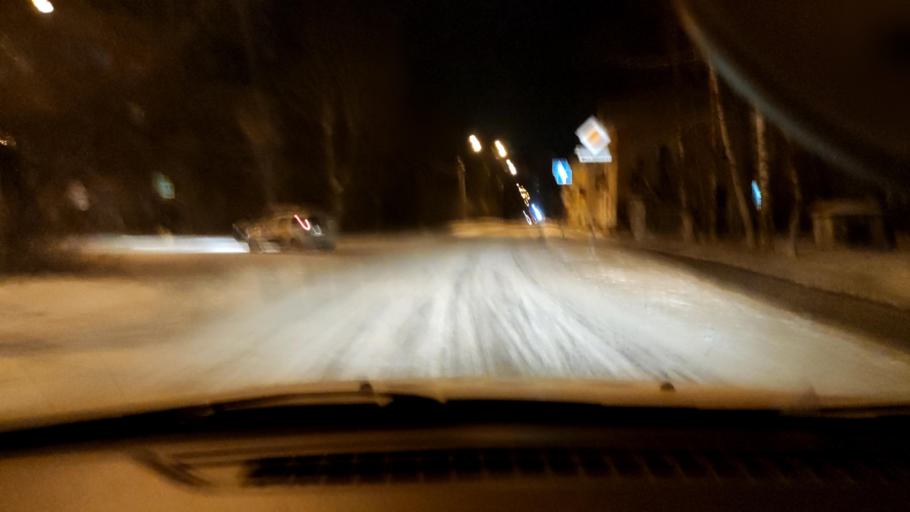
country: RU
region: Perm
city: Kultayevo
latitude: 58.0059
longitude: 55.9609
